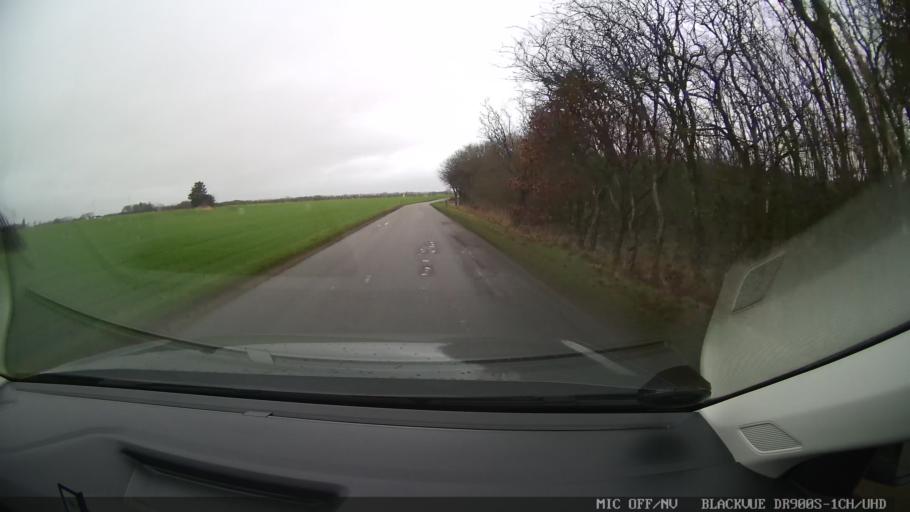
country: DK
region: Central Jutland
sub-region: Viborg Kommune
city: Karup
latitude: 56.3340
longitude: 9.2696
